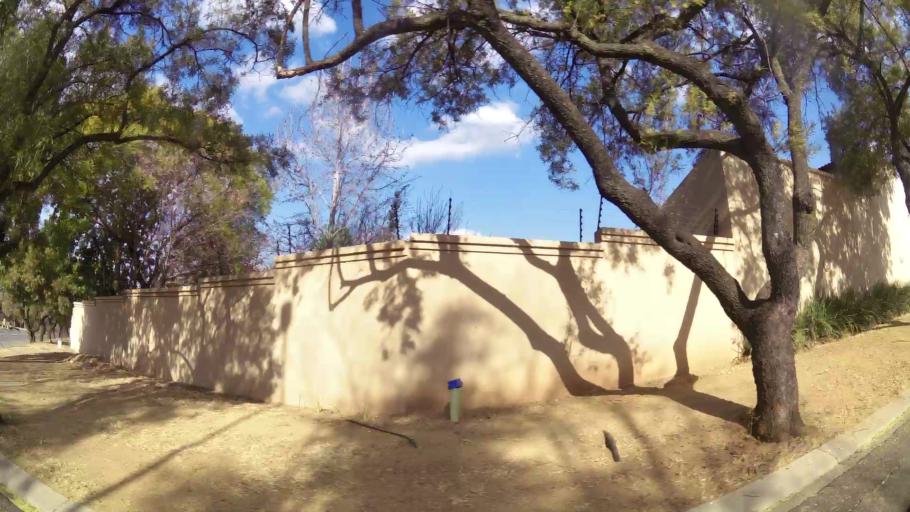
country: ZA
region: Gauteng
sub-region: City of Johannesburg Metropolitan Municipality
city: Diepsloot
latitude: -26.0075
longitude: 28.0250
